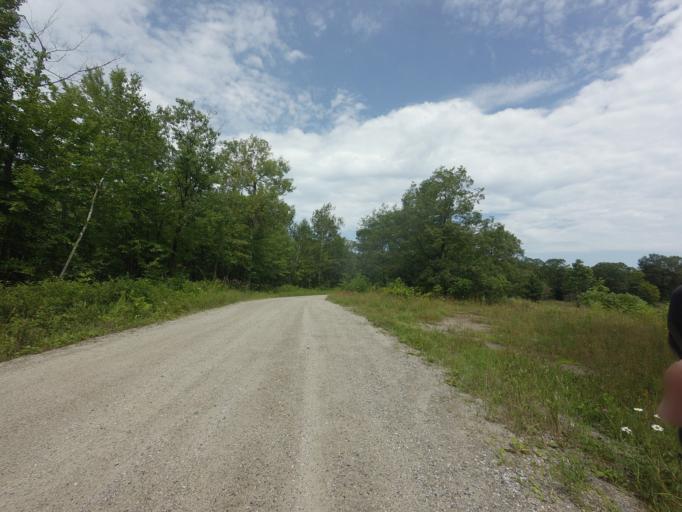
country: CA
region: Ontario
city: Perth
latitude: 44.7584
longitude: -76.6130
